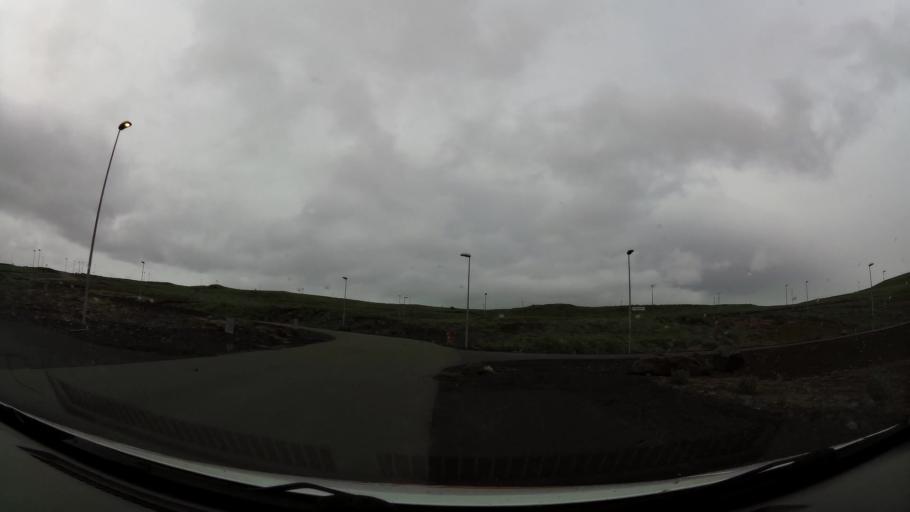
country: IS
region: Capital Region
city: Hafnarfjoerdur
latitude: 64.0460
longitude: -21.9574
